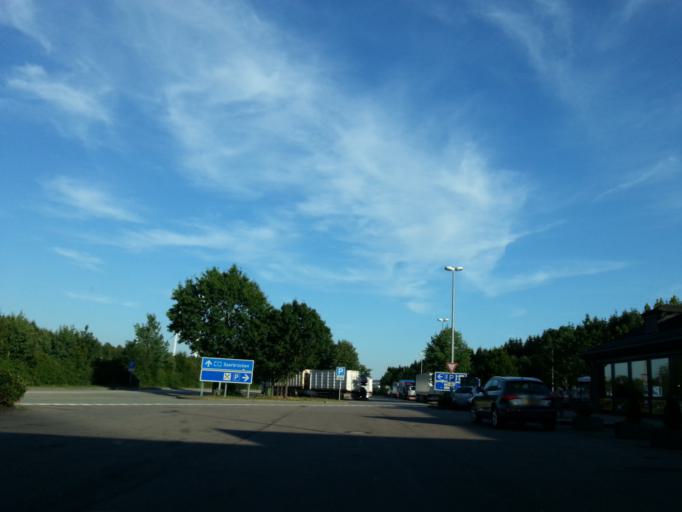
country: DE
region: Rheinland-Pfalz
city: Hinzert-Polert
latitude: 49.6911
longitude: 6.8963
